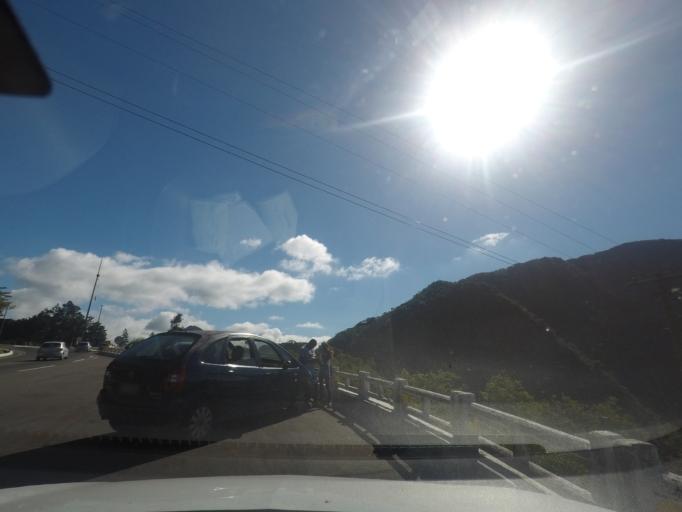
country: BR
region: Rio de Janeiro
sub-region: Teresopolis
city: Teresopolis
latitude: -22.4633
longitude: -42.9883
